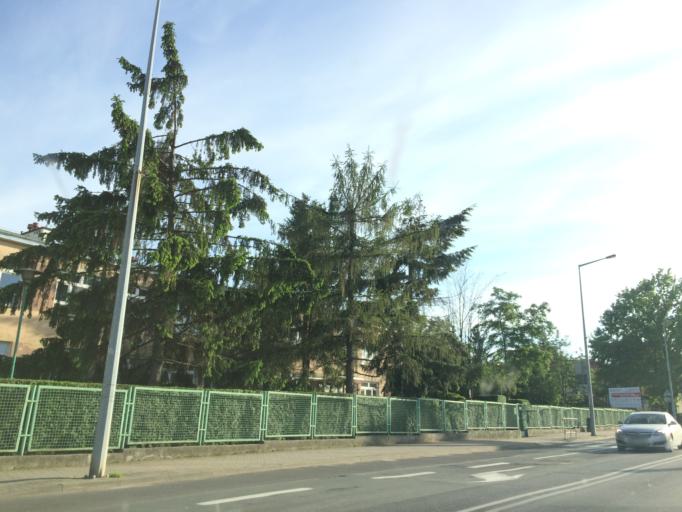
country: PL
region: Lower Silesian Voivodeship
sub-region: Powiat swidnicki
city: Swidnica
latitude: 50.8443
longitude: 16.4715
